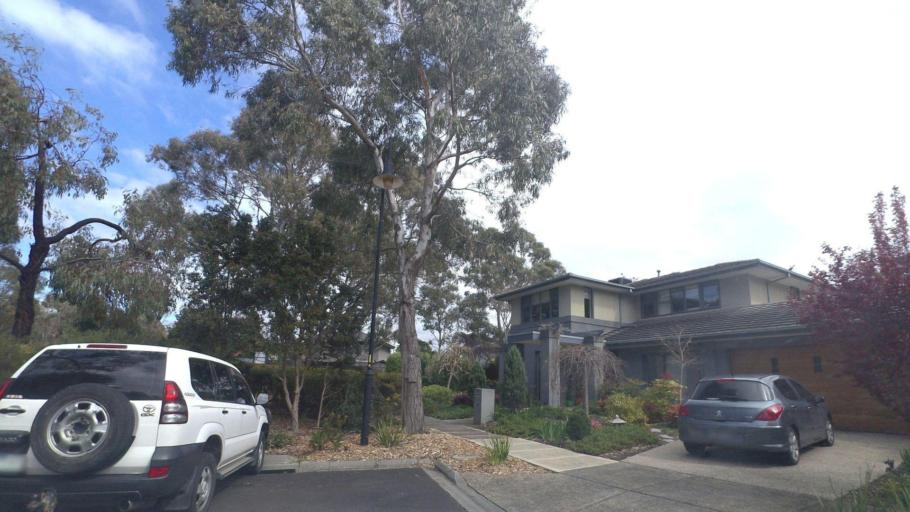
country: AU
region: Victoria
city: Macleod
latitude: -37.7190
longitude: 145.0639
